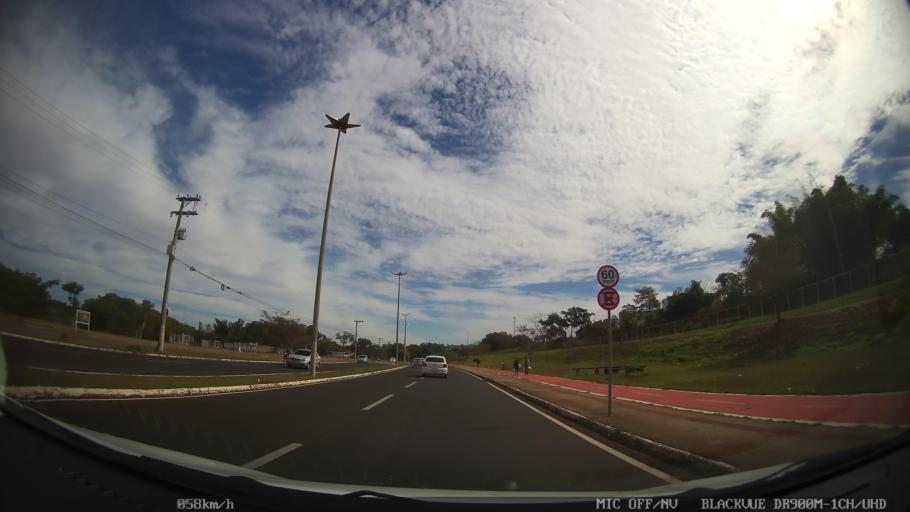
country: BR
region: Sao Paulo
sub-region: Catanduva
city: Catanduva
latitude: -21.1422
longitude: -48.9534
